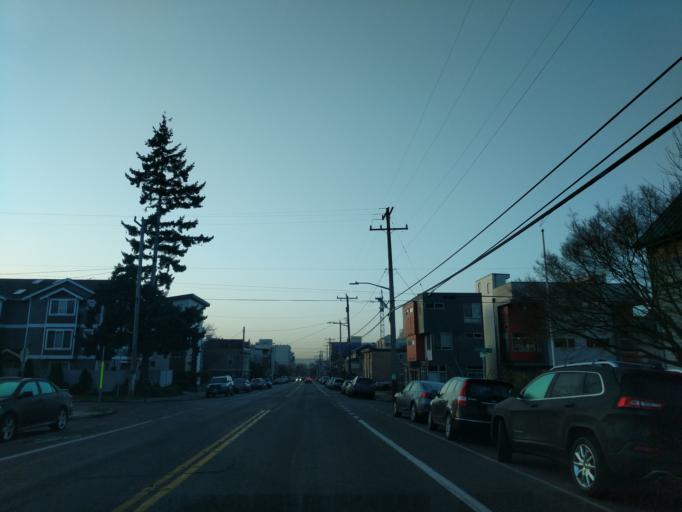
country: US
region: Washington
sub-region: King County
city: Seattle
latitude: 47.6726
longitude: -122.3822
